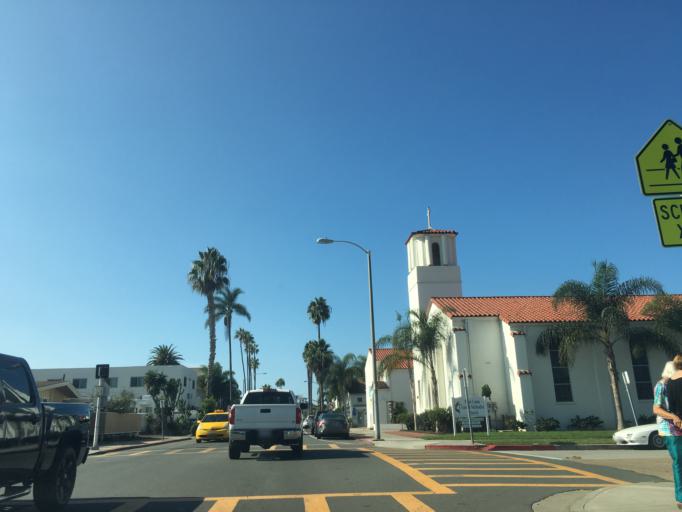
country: US
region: California
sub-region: San Diego County
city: Coronado
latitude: 32.7466
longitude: -117.2460
